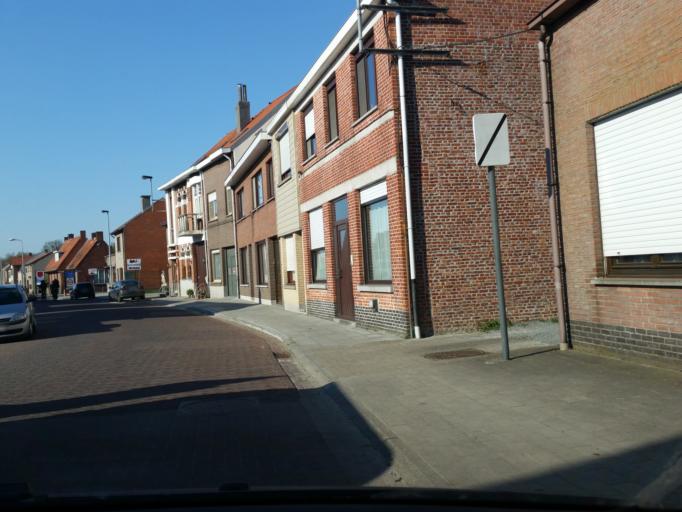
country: NL
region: Zeeland
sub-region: Gemeente Hulst
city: Hulst
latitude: 51.2591
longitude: 4.0911
